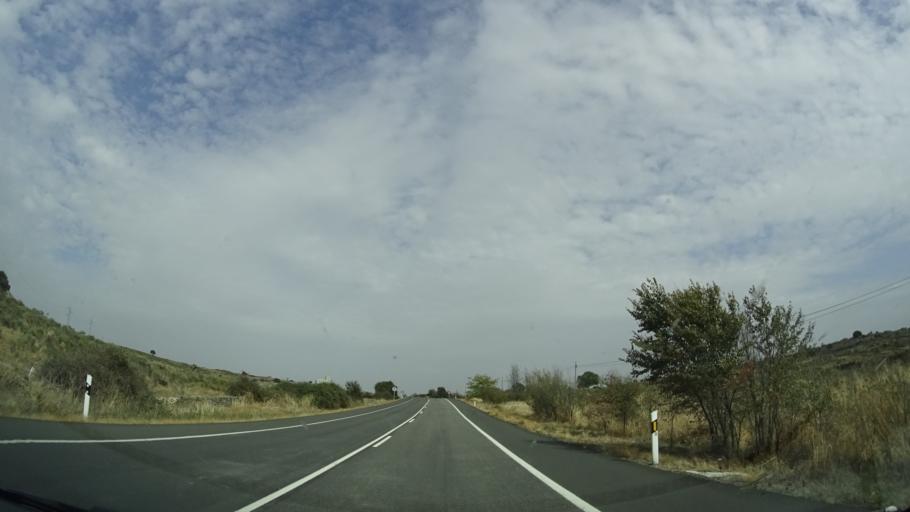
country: ES
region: Extremadura
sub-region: Provincia de Caceres
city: Trujillo
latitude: 39.4408
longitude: -5.8867
